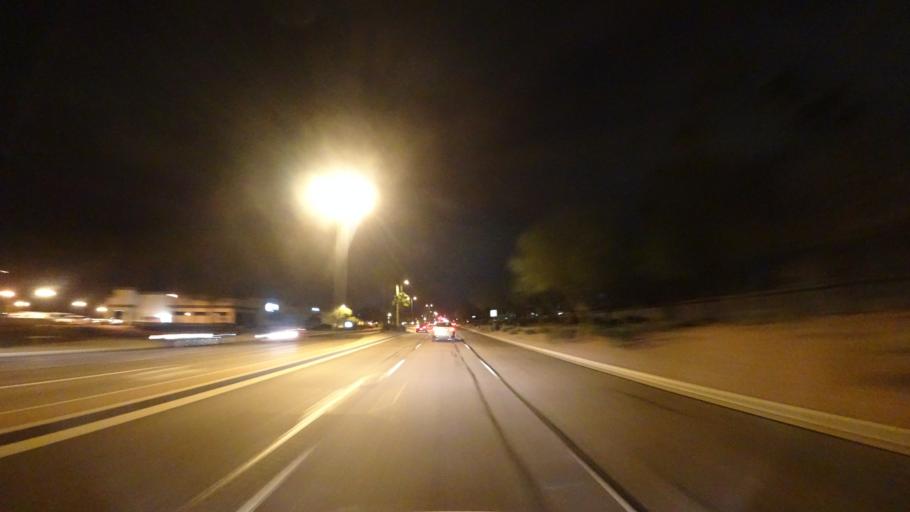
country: US
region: Arizona
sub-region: Maricopa County
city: Gilbert
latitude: 33.3693
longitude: -111.7565
